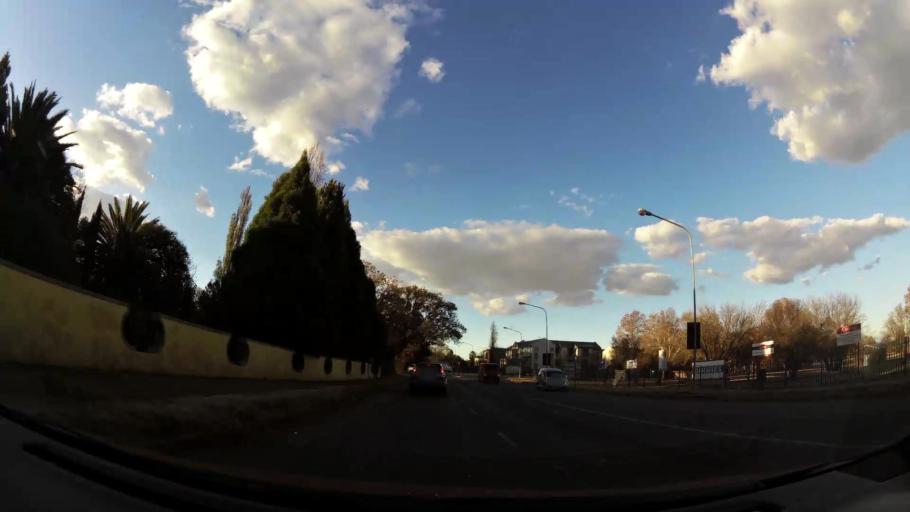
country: ZA
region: North-West
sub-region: Dr Kenneth Kaunda District Municipality
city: Potchefstroom
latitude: -26.6842
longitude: 27.1010
